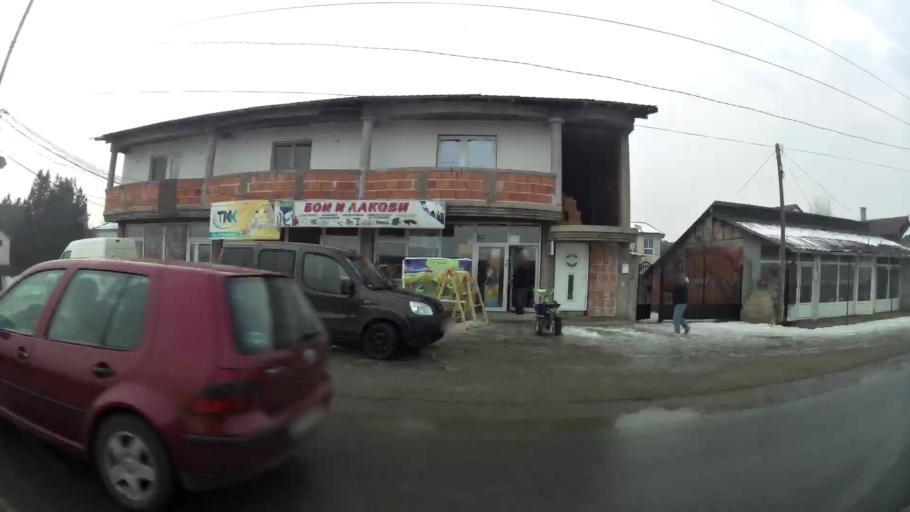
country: MK
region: Ilinden
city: Jurumleri
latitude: 41.9791
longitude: 21.5300
